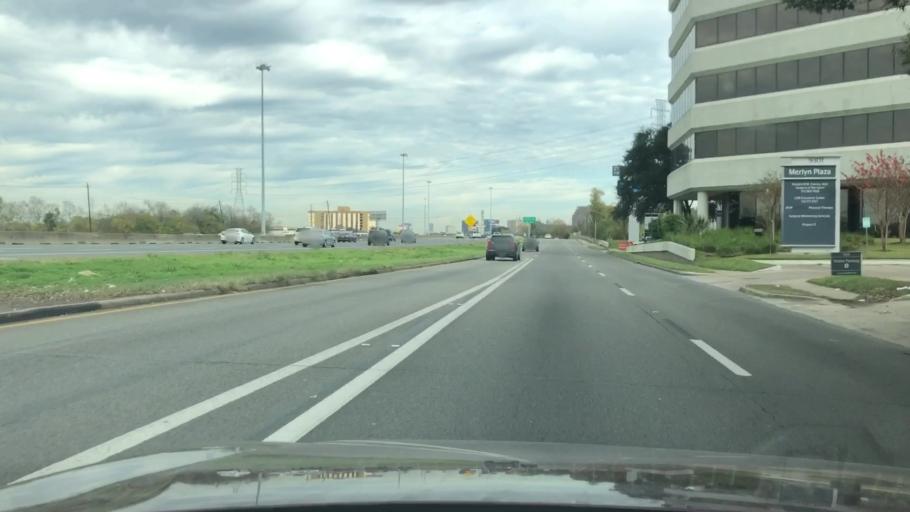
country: US
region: Texas
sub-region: Fort Bend County
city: Meadows Place
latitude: 29.6790
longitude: -95.5381
